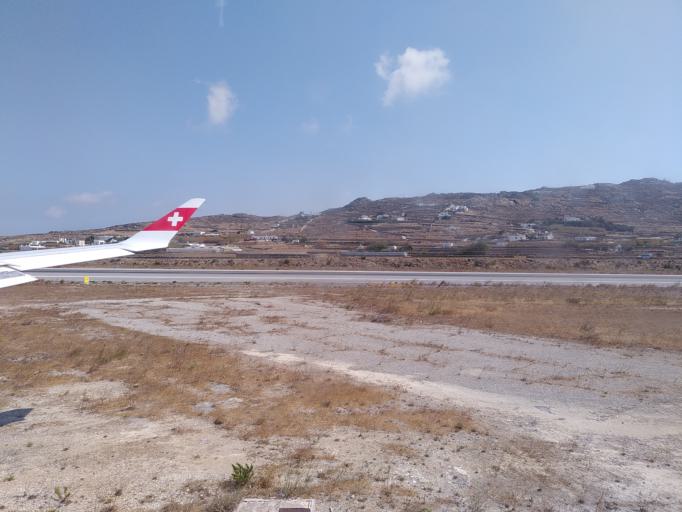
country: GR
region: South Aegean
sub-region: Nomos Kykladon
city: Mykonos
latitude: 37.4354
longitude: 25.3471
